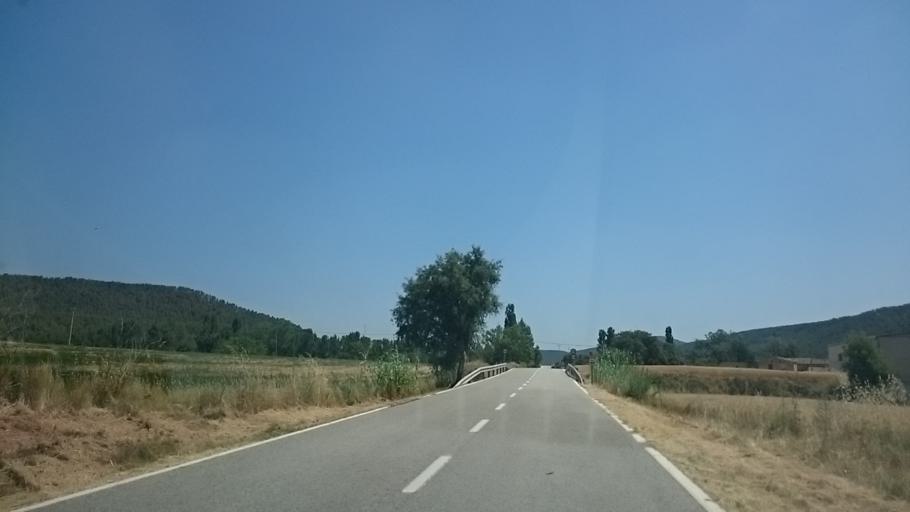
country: ES
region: Catalonia
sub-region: Provincia de Barcelona
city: Sant Marti de Tous
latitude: 41.4883
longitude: 1.5094
